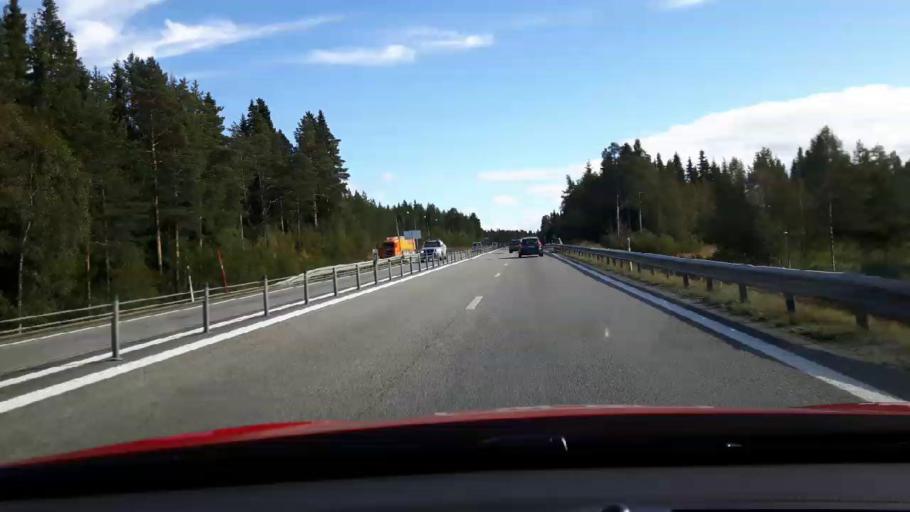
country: SE
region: Jaemtland
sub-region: OEstersunds Kommun
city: Ostersund
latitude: 63.1757
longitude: 14.6966
